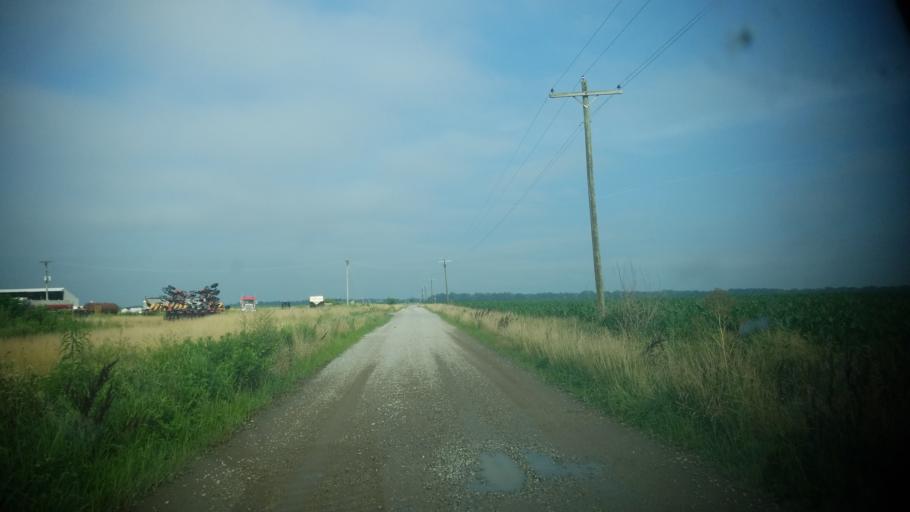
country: US
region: Illinois
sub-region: Clay County
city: Flora
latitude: 38.6015
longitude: -88.3419
